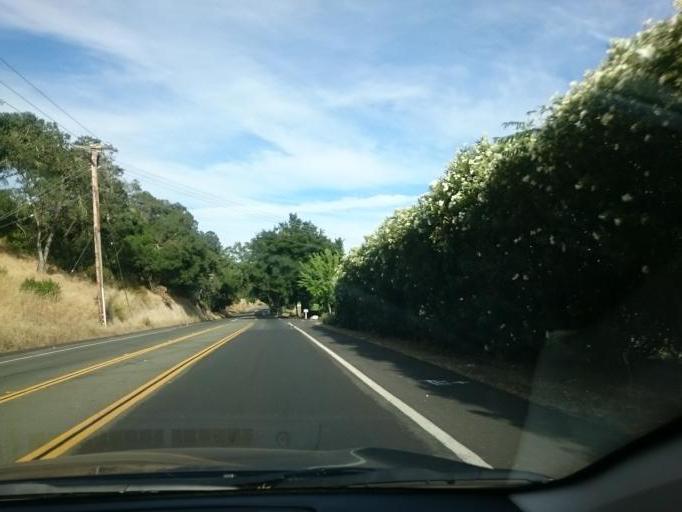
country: US
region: California
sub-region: Napa County
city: Saint Helena
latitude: 38.5061
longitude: -122.4403
